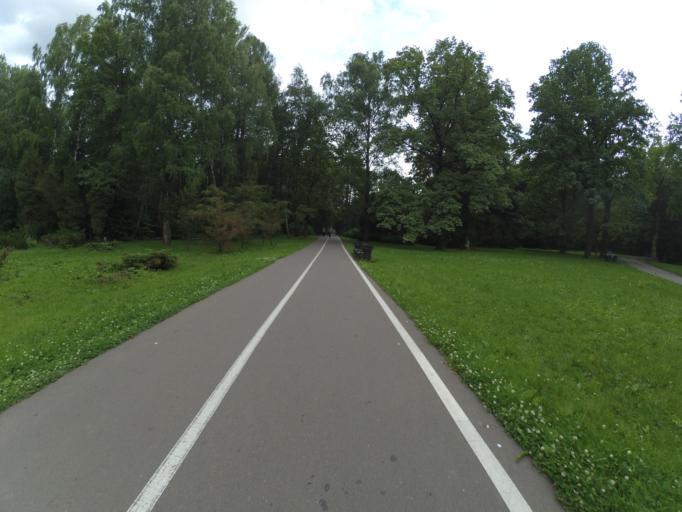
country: RU
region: Moscow
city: Ostankinskiy
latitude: 55.8415
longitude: 37.6101
